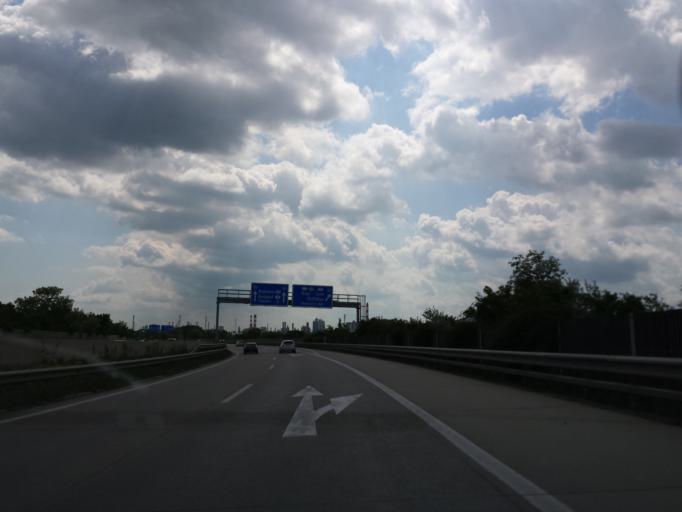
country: AT
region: Lower Austria
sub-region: Politischer Bezirk Wien-Umgebung
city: Schwechat
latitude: 48.1536
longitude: 16.4806
